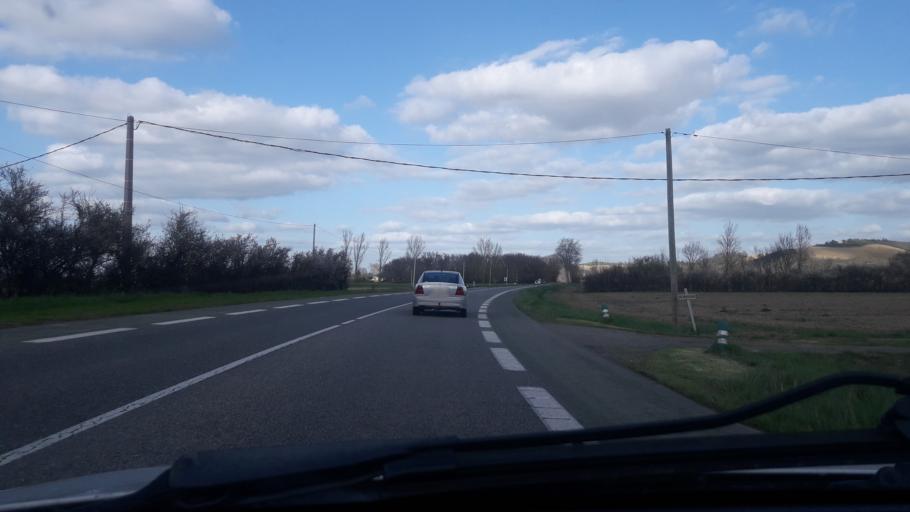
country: FR
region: Midi-Pyrenees
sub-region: Departement de la Haute-Garonne
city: Rieux-Volvestre
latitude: 43.2725
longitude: 1.1997
